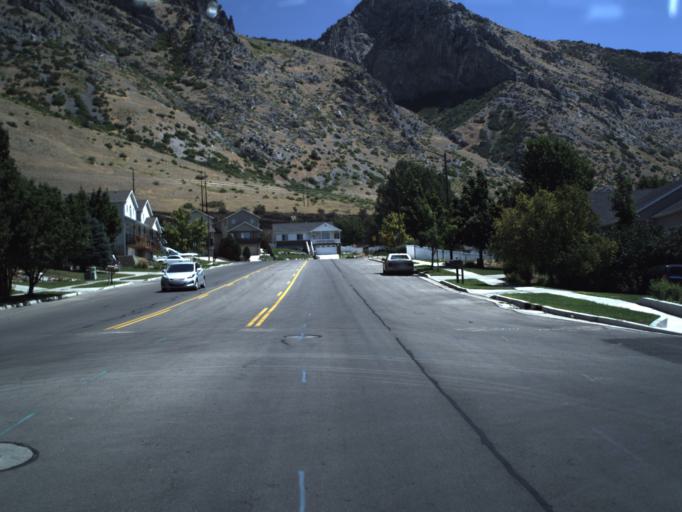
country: US
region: Utah
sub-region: Utah County
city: Springville
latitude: 40.1857
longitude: -111.6085
